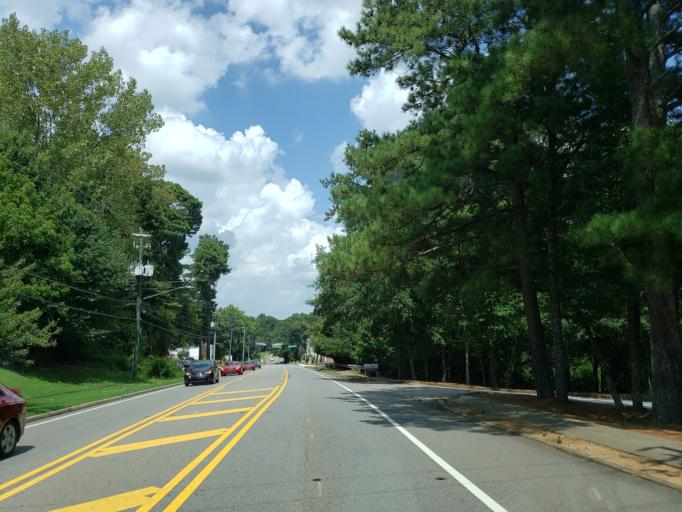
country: US
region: Georgia
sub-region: Fulton County
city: Roswell
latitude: 34.0350
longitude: -84.3386
